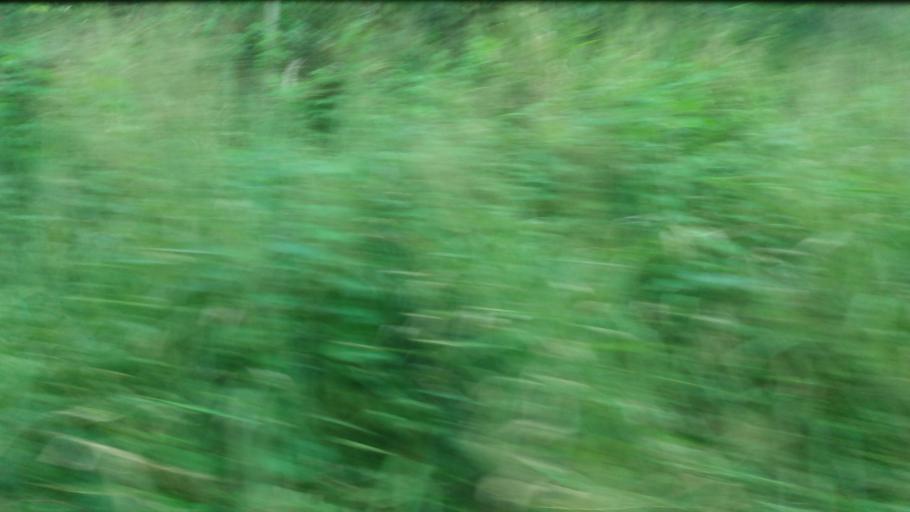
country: BR
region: Pernambuco
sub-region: Catende
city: Catende
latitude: -8.6944
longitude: -35.7286
